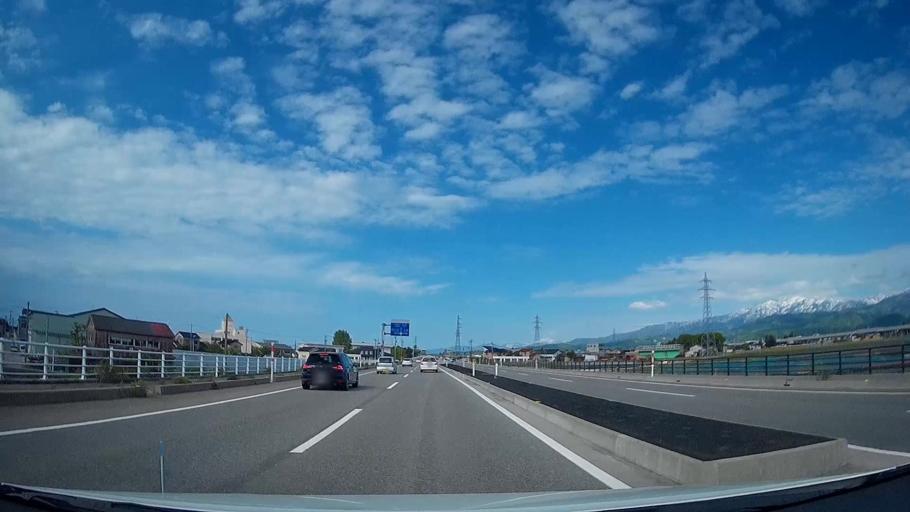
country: JP
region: Toyama
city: Namerikawa
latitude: 36.7610
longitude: 137.3666
